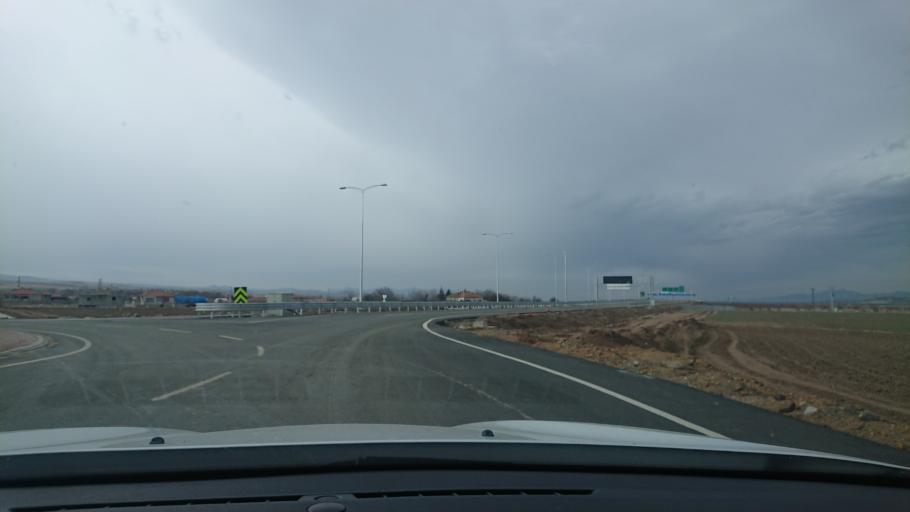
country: TR
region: Aksaray
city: Agacoren
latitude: 38.9318
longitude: 33.9699
